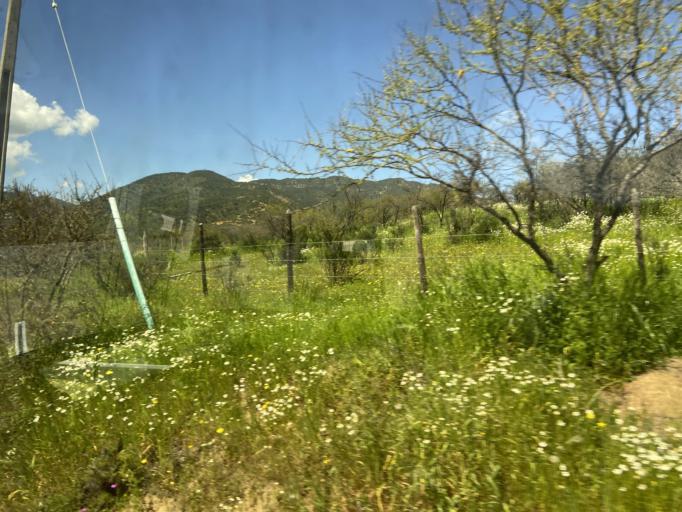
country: CL
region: Valparaiso
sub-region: Provincia de Marga Marga
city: Villa Alemana
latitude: -33.1846
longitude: -71.2997
